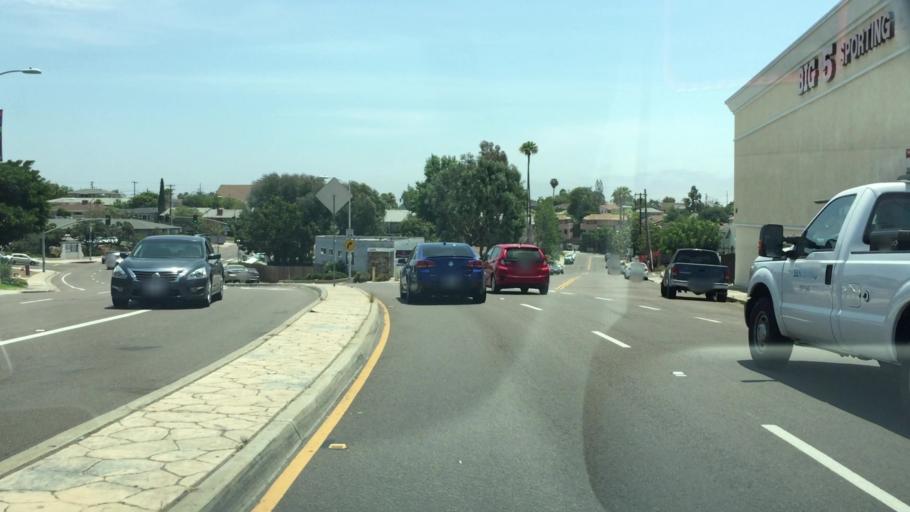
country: US
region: California
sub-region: San Diego County
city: Lemon Grove
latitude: 32.7608
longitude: -117.0671
